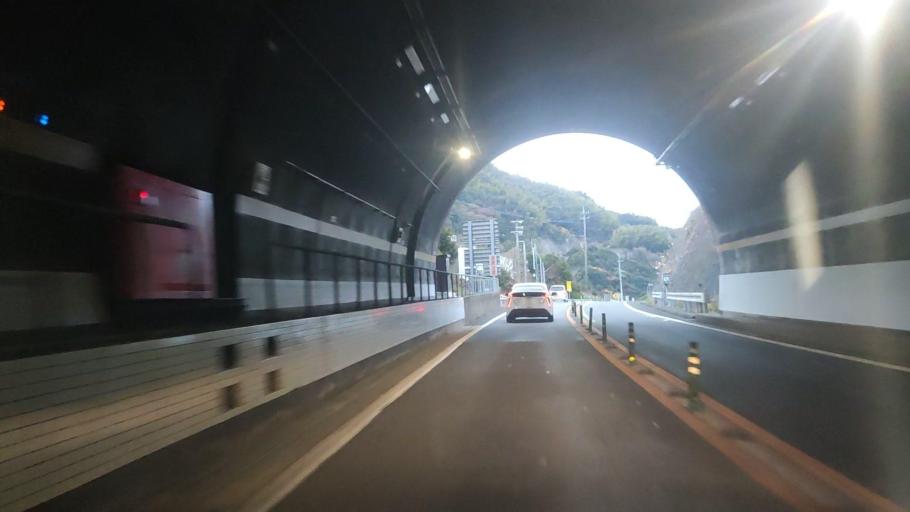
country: JP
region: Nagasaki
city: Nagasaki-shi
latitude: 32.7717
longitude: 129.8907
